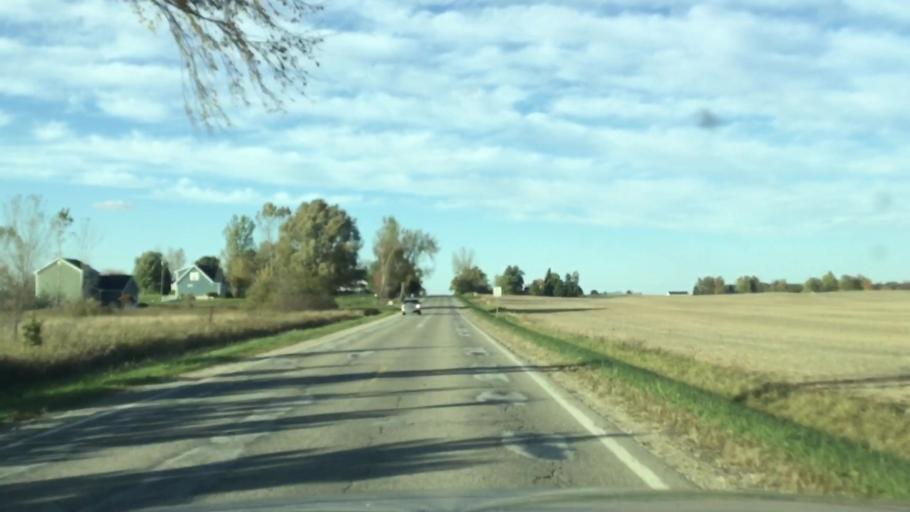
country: US
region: Michigan
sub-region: Lapeer County
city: North Branch
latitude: 43.2610
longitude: -83.1979
